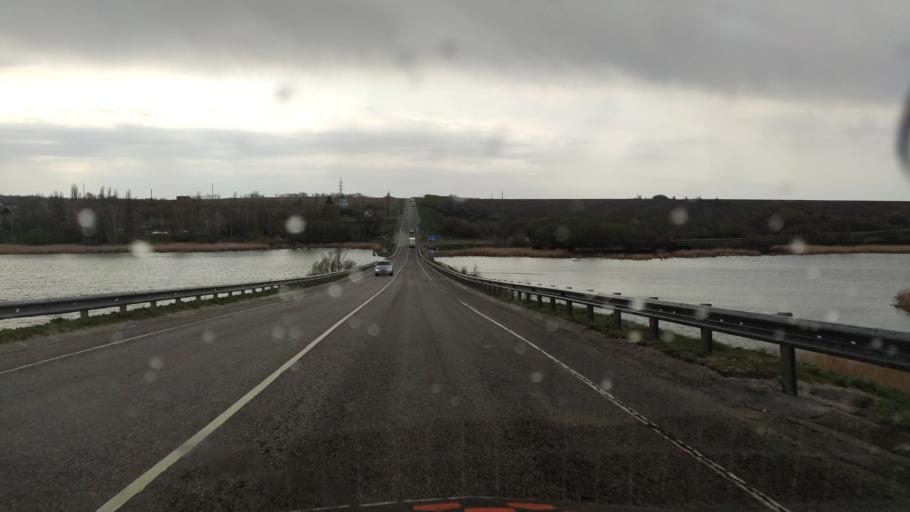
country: RU
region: Voronezj
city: Nizhnedevitsk
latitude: 51.5645
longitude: 38.3716
